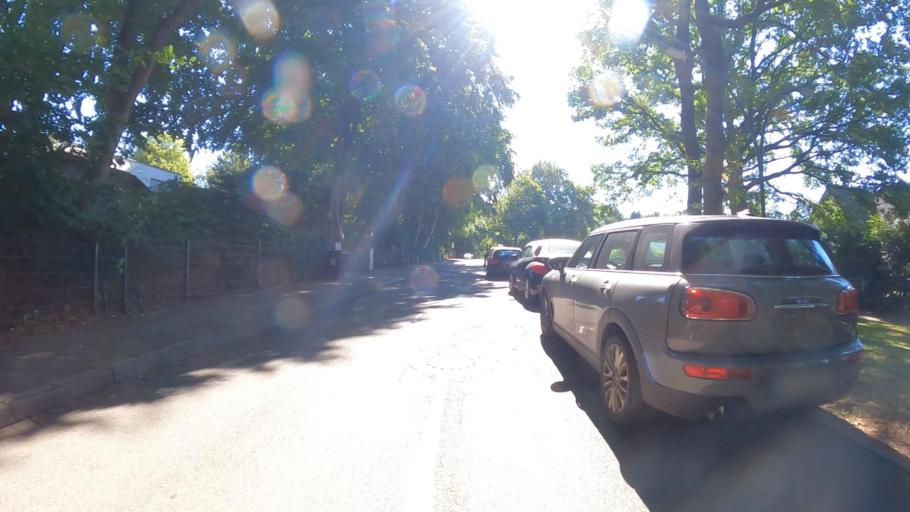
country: DE
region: Schleswig-Holstein
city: Aumuhle
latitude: 53.5218
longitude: 10.3228
